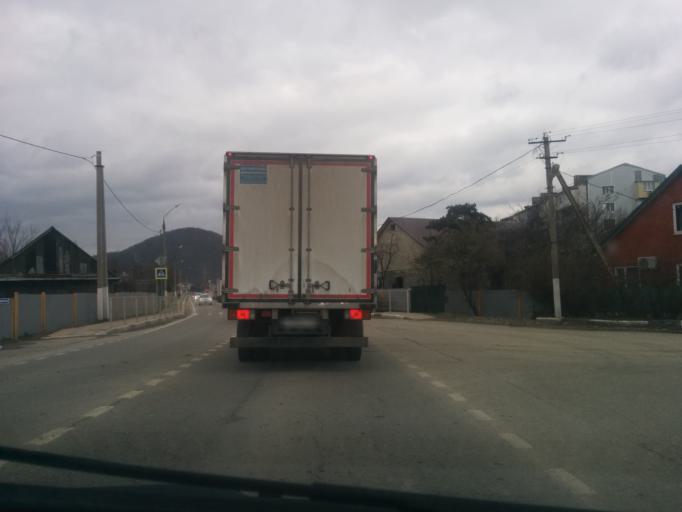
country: RU
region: Krasnodarskiy
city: Novomikhaylovskiy
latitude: 44.2567
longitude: 38.8553
